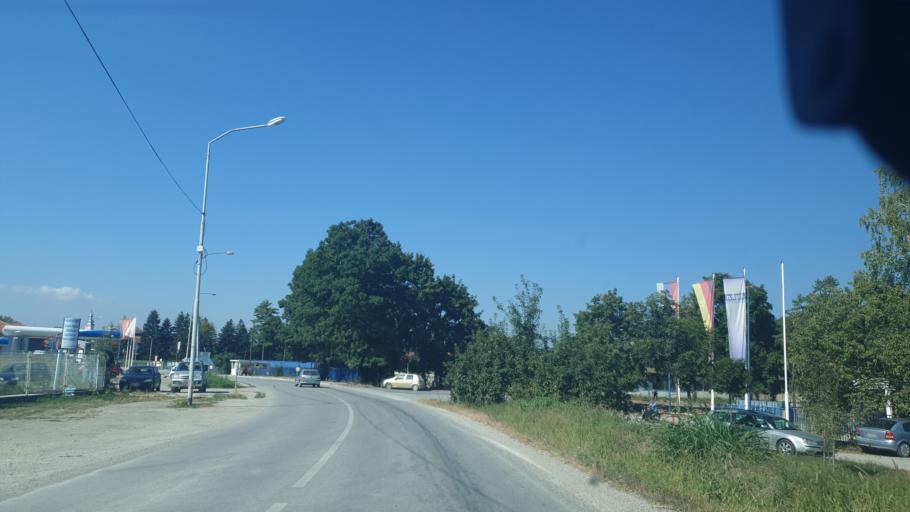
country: RS
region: Central Serbia
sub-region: Kolubarski Okrug
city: Mionica
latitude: 44.2552
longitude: 20.0937
